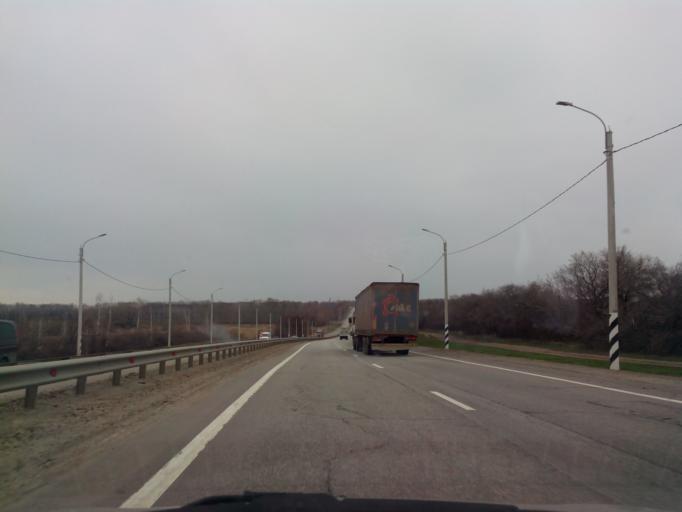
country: RU
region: Tambov
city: Selezni
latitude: 52.7438
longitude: 41.2016
